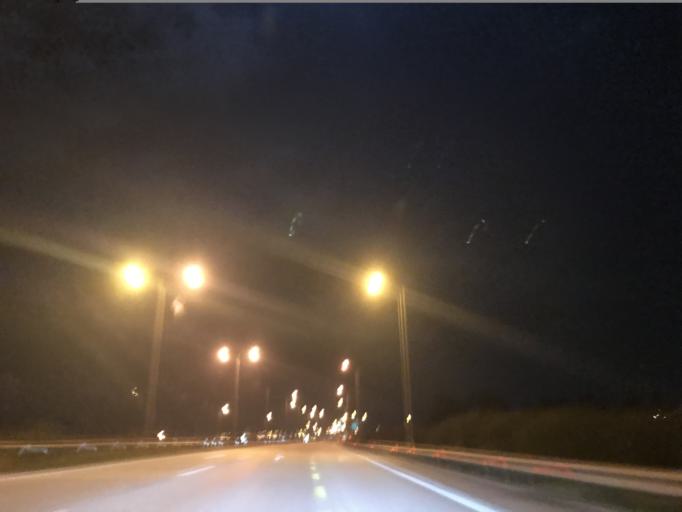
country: TR
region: Hatay
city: Mahmutlar
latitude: 36.9637
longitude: 36.1139
